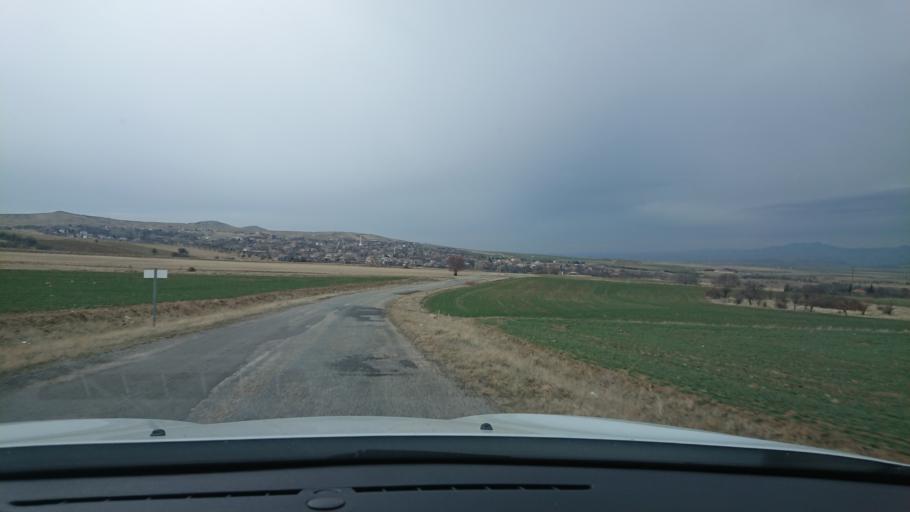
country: TR
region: Aksaray
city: Sariyahsi
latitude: 38.9519
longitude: 33.9001
